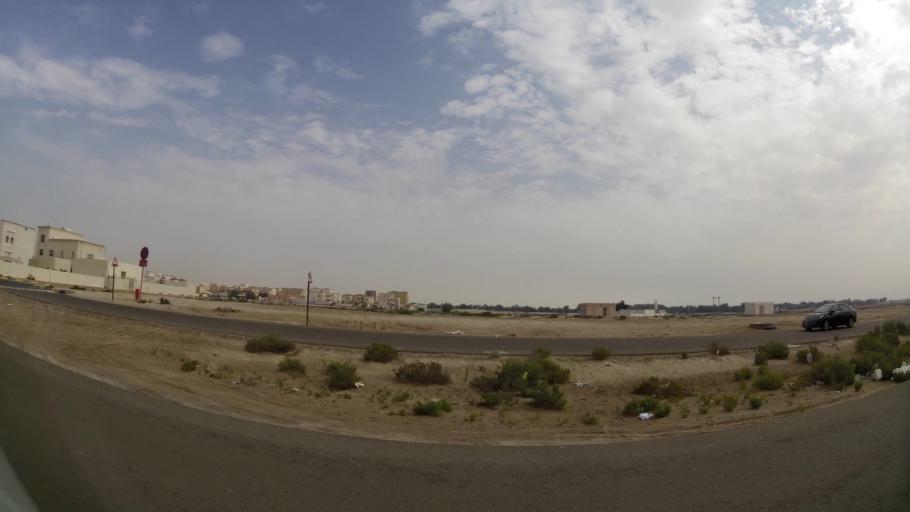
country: AE
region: Abu Dhabi
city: Abu Dhabi
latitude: 24.3046
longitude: 54.6576
